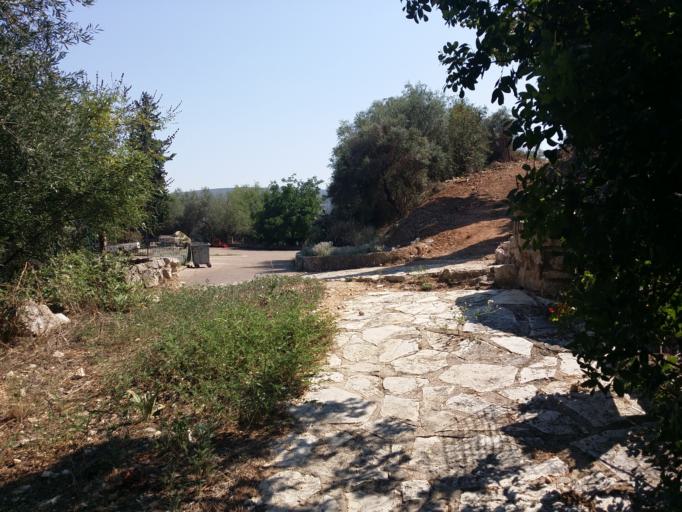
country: GR
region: West Greece
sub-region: Nomos Aitolias kai Akarnanias
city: Vonitsa
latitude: 38.9201
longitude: 20.8857
